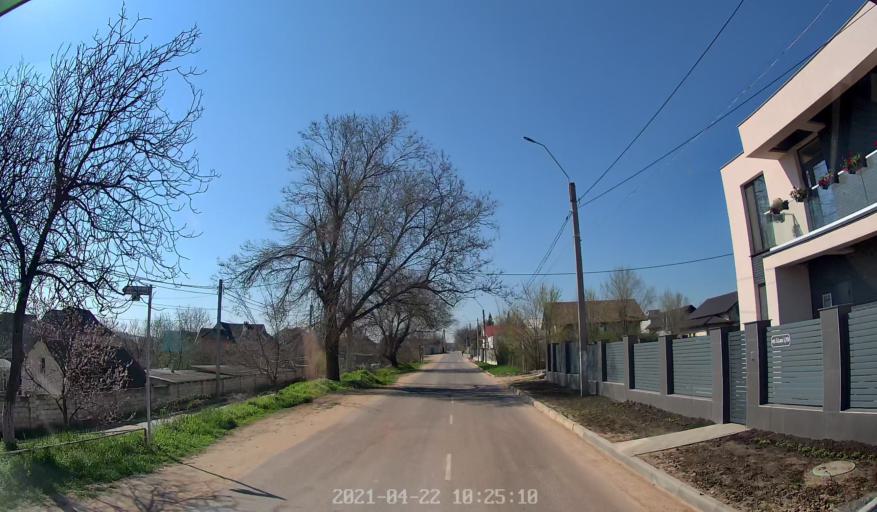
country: MD
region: Chisinau
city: Ciorescu
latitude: 47.1250
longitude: 28.8845
